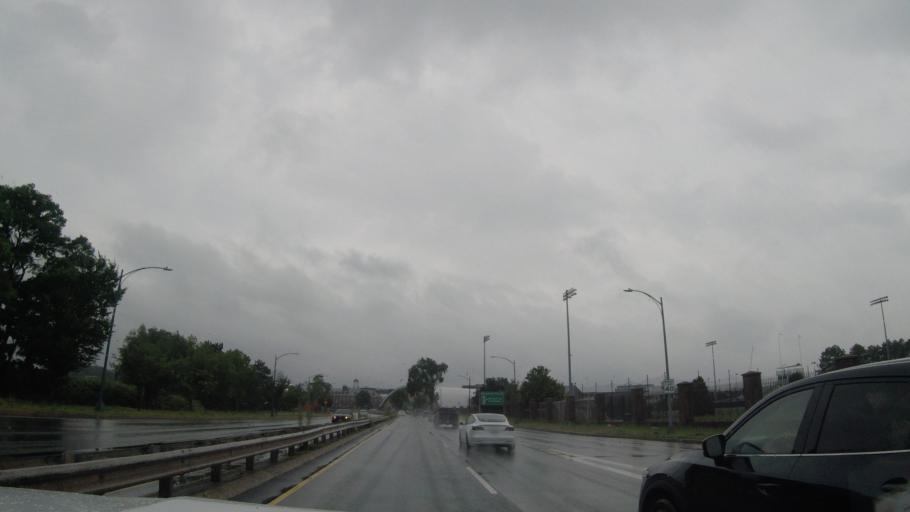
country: US
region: Massachusetts
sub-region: Middlesex County
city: Cambridge
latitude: 42.3715
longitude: -71.1270
